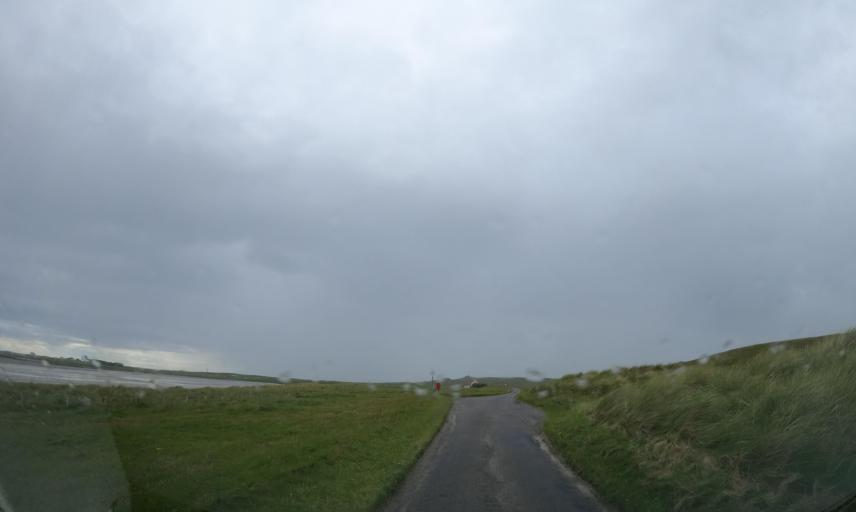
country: GB
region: Scotland
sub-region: Eilean Siar
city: Barra
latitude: 56.5164
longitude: -6.8142
